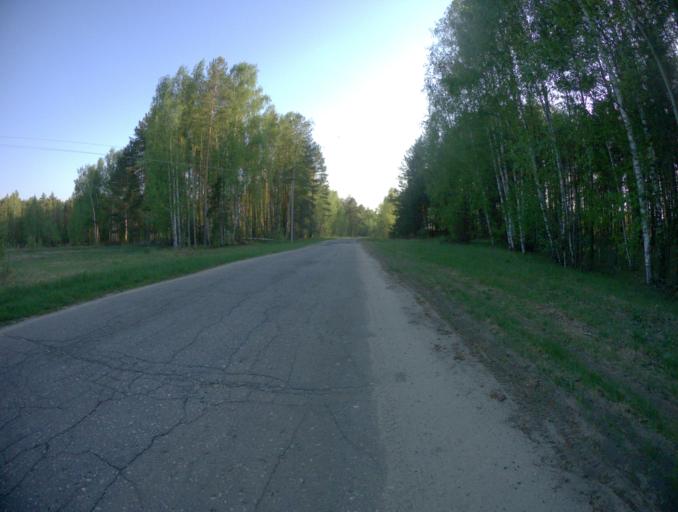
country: RU
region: Vladimir
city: Vyazniki
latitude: 56.3369
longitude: 42.1335
